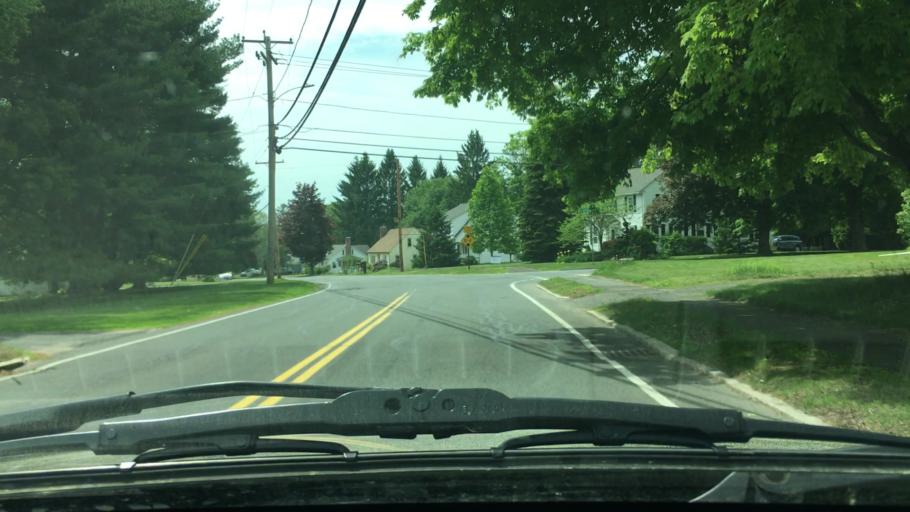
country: US
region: Massachusetts
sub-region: Hampshire County
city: Belchertown
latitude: 42.2716
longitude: -72.3982
